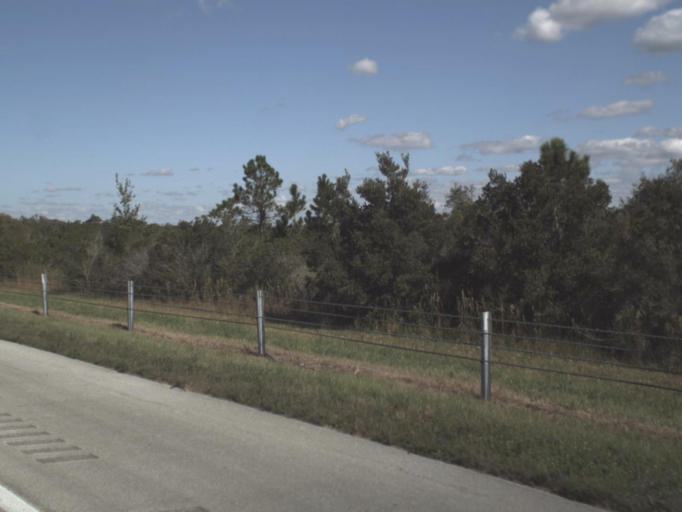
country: US
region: Florida
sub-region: Osceola County
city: Saint Cloud
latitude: 27.9243
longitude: -81.0611
